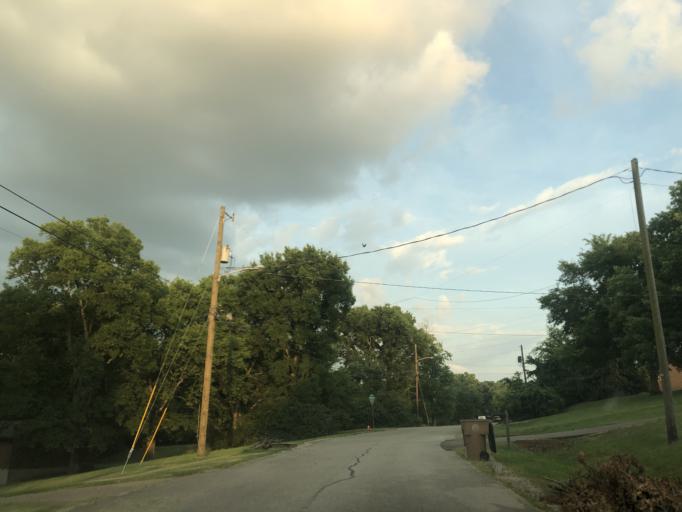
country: US
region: Tennessee
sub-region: Davidson County
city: Nashville
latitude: 36.1606
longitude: -86.7155
